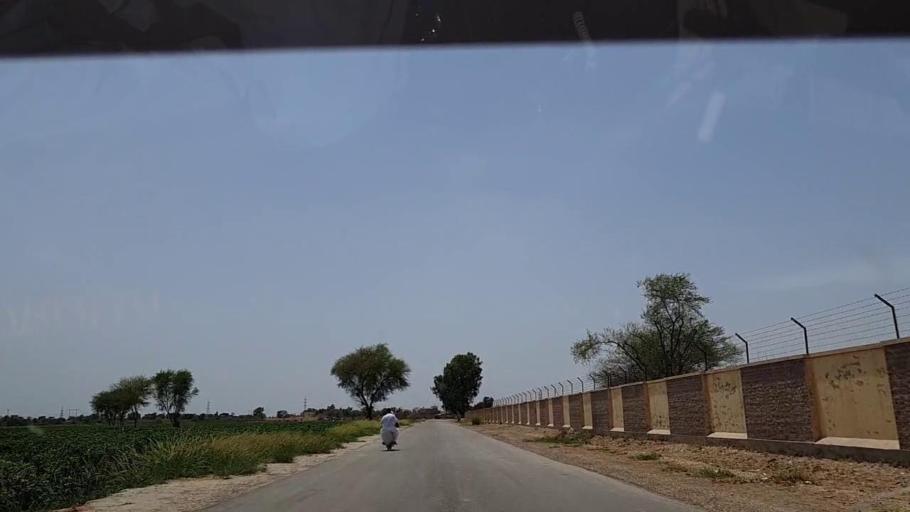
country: PK
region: Sindh
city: Dadu
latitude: 26.7147
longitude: 67.7409
